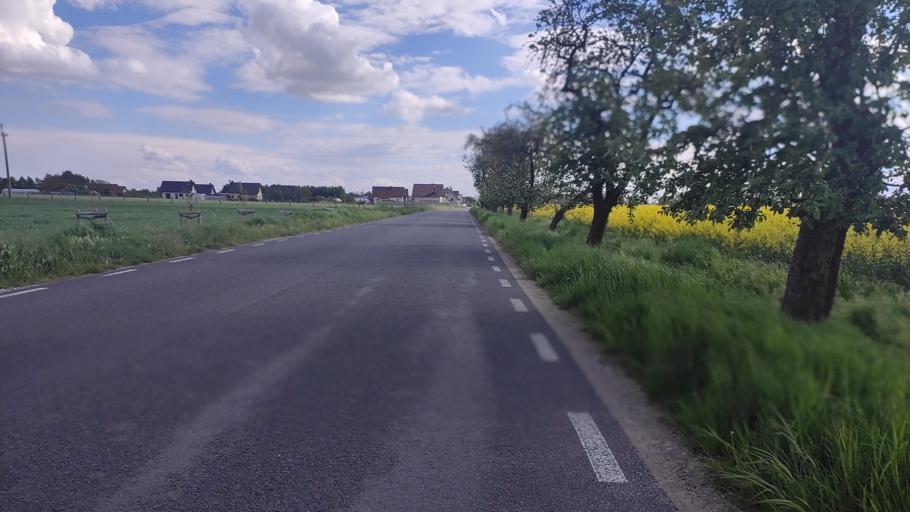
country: PL
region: Greater Poland Voivodeship
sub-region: Powiat poznanski
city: Kostrzyn
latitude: 52.4078
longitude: 17.1666
